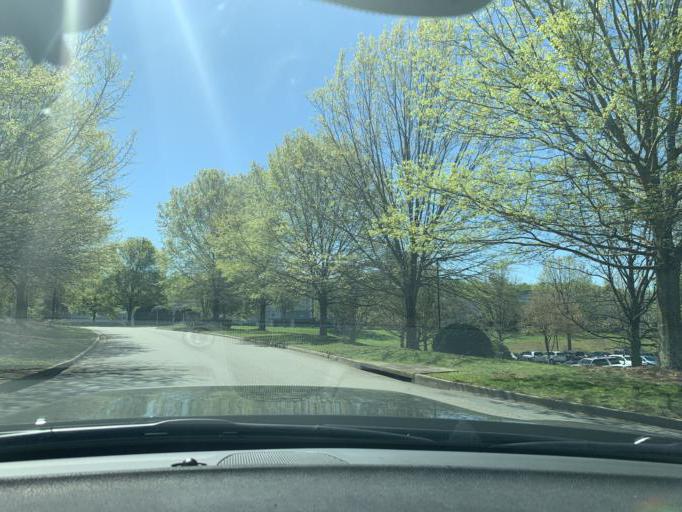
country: US
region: Georgia
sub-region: Fulton County
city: Johns Creek
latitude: 34.1199
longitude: -84.2084
